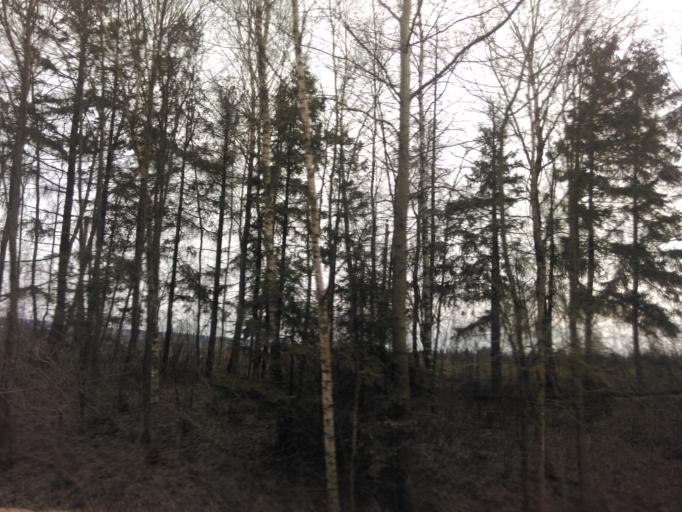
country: RU
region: Moskovskaya
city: Tuchkovo
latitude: 55.6105
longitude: 36.4983
